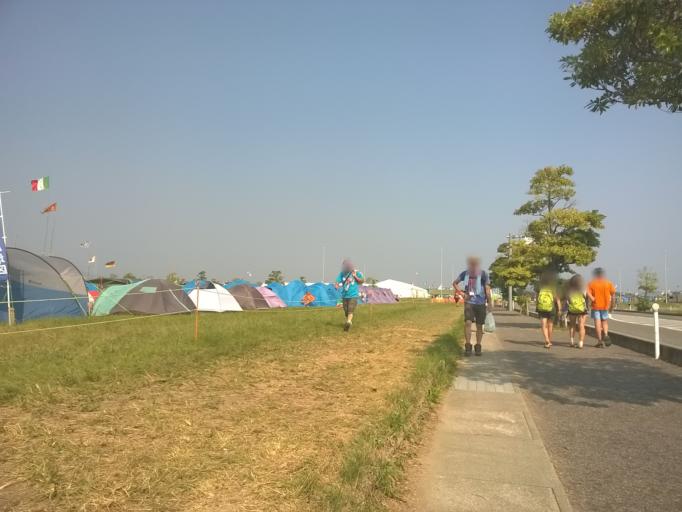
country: JP
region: Yamaguchi
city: Ogori-shimogo
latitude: 34.0165
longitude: 131.3748
